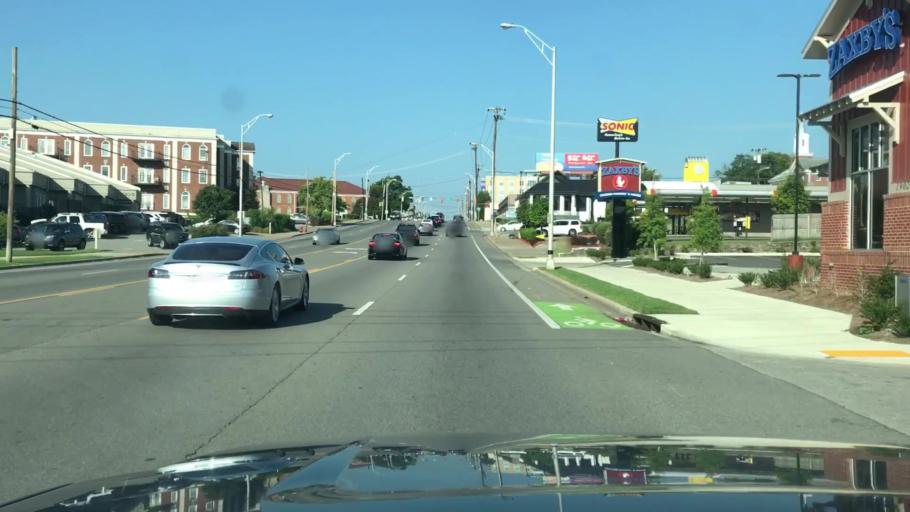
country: US
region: Tennessee
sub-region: Davidson County
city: Nashville
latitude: 36.1576
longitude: -86.8016
